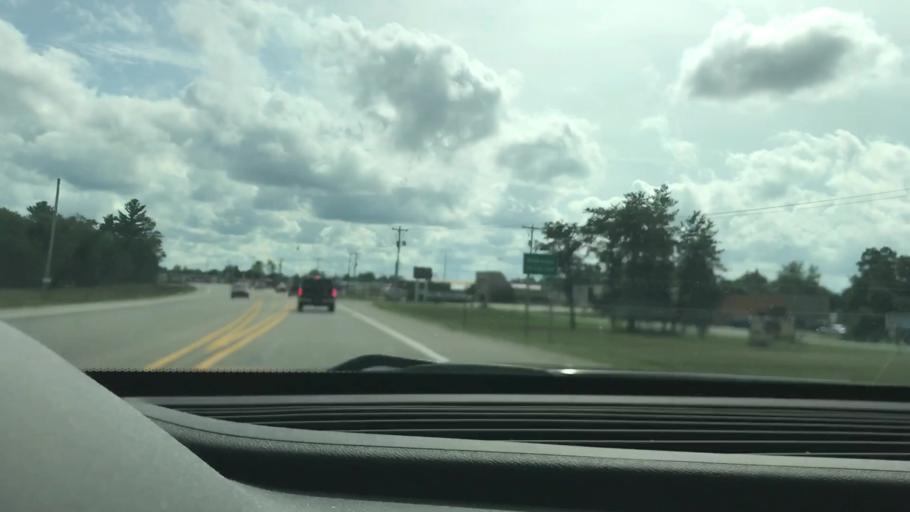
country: US
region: Michigan
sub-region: Kalkaska County
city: Kalkaska
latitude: 44.7484
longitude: -85.1736
